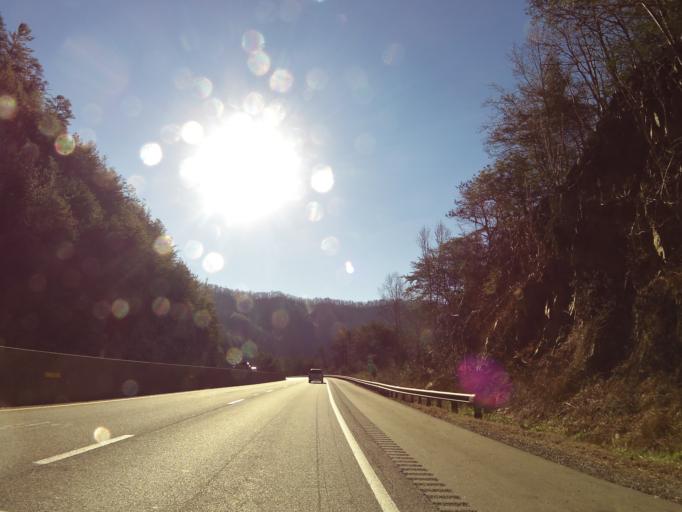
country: US
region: North Carolina
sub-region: Haywood County
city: Cove Creek
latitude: 35.7155
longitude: -83.0330
